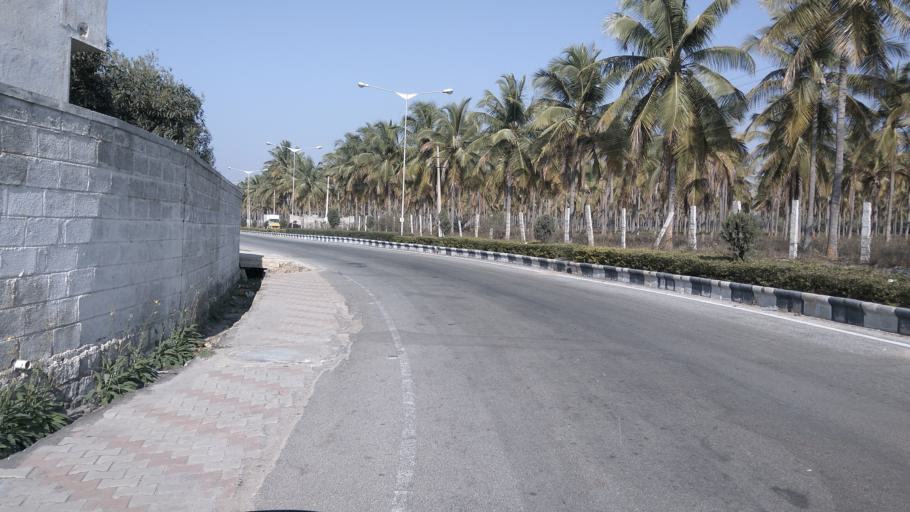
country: IN
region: Karnataka
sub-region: Bangalore Rural
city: Devanhalli
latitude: 13.1984
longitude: 77.6411
